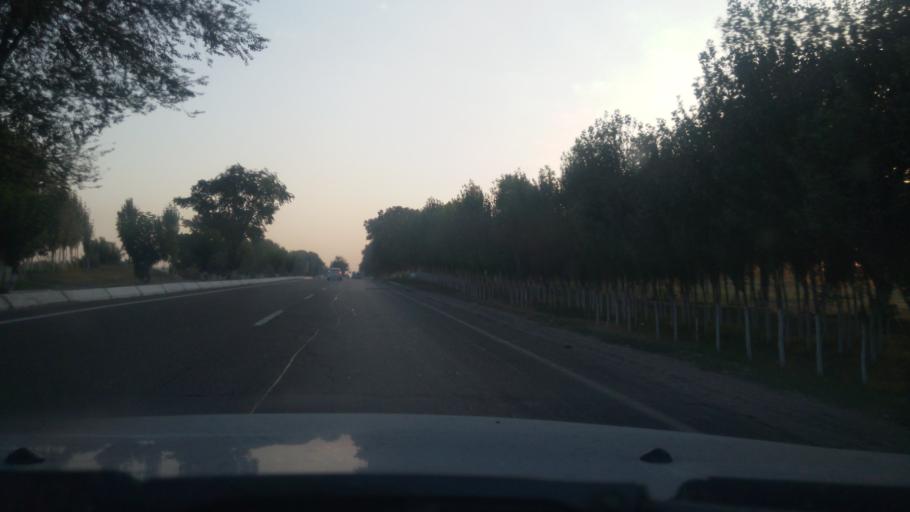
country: UZ
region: Toshkent
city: Yangiyul
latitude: 41.1355
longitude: 69.0156
